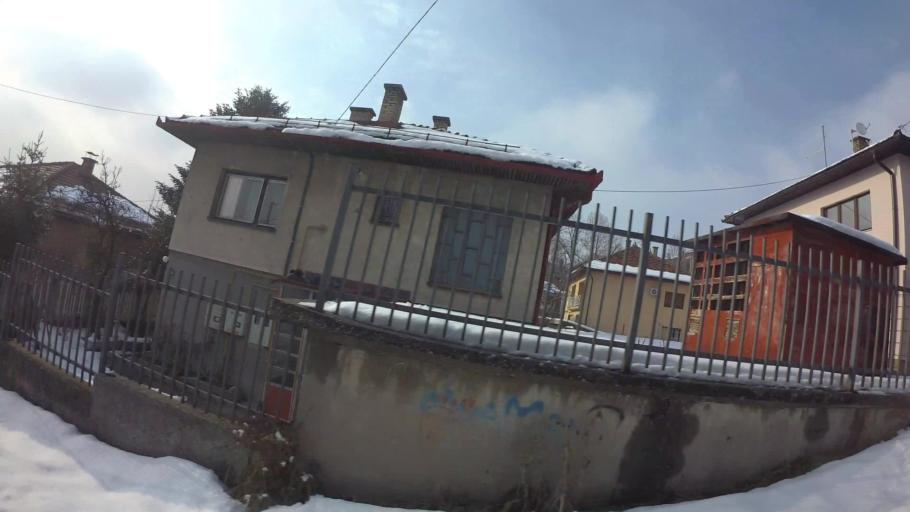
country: BA
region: Federation of Bosnia and Herzegovina
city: Kobilja Glava
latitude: 43.8699
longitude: 18.4294
